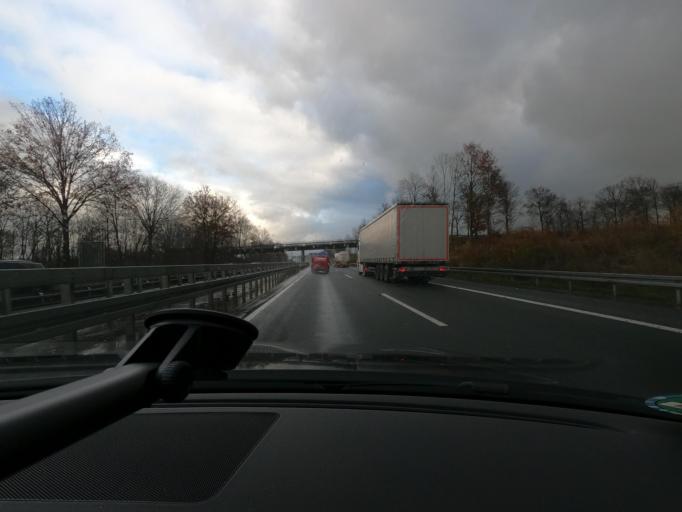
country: DE
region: North Rhine-Westphalia
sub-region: Regierungsbezirk Arnsberg
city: Unna
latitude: 51.5209
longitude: 7.6959
